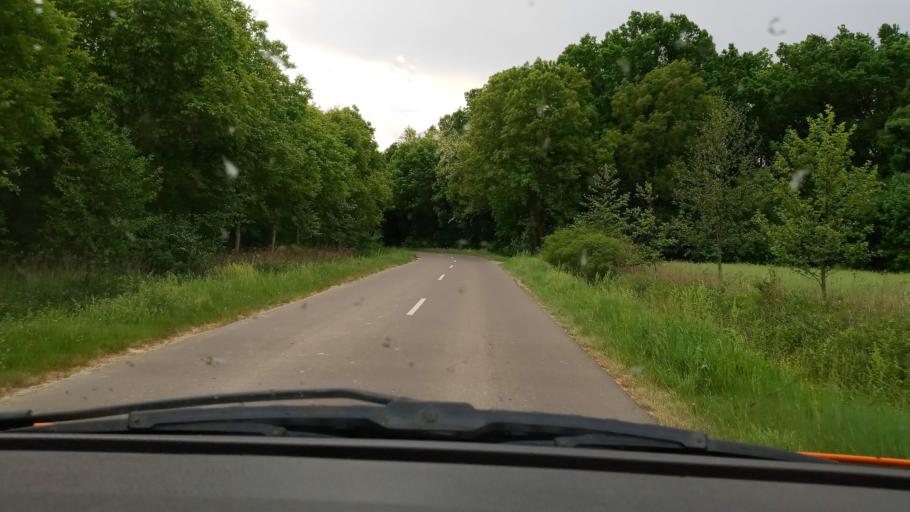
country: HU
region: Baranya
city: Vajszlo
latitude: 45.8337
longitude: 17.9728
